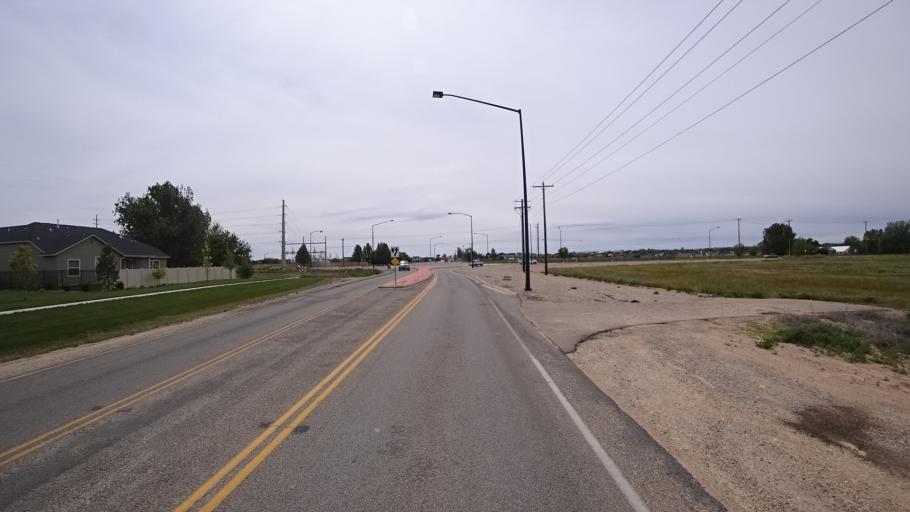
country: US
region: Idaho
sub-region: Ada County
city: Meridian
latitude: 43.5623
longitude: -116.3546
